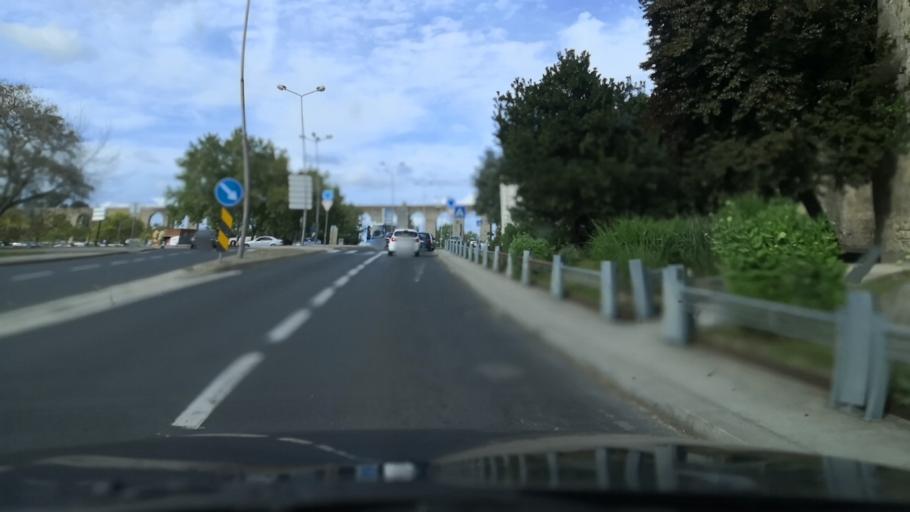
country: PT
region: Evora
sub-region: Evora
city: Evora
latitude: 38.5751
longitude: -7.9148
